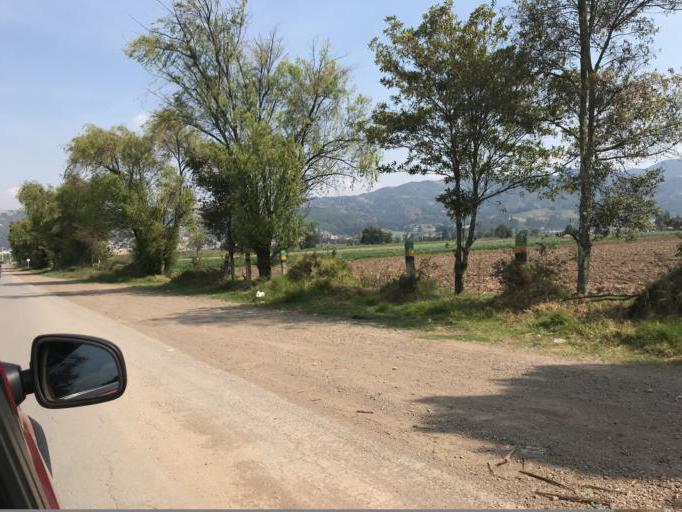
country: CO
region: Boyaca
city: Samaca
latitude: 5.5034
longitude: -73.4973
